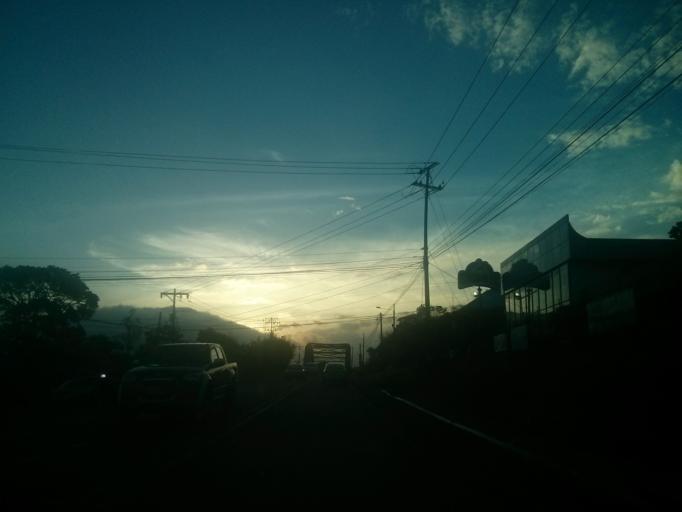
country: CR
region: Cartago
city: Cartago
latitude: 9.8806
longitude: -83.9189
